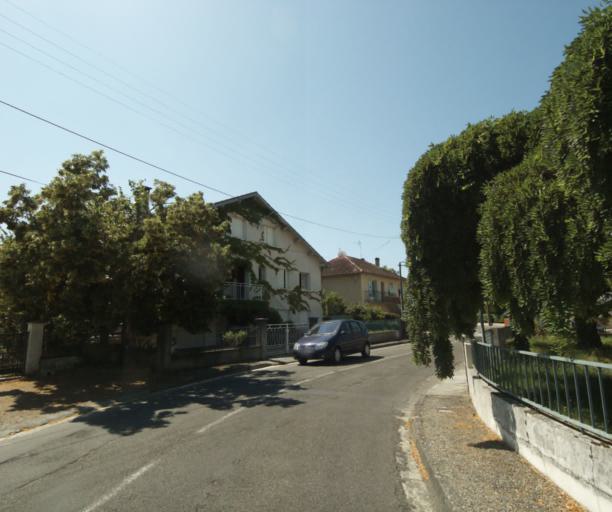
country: FR
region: Midi-Pyrenees
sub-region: Departement du Tarn-et-Garonne
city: Montauban
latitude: 44.0274
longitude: 1.3594
